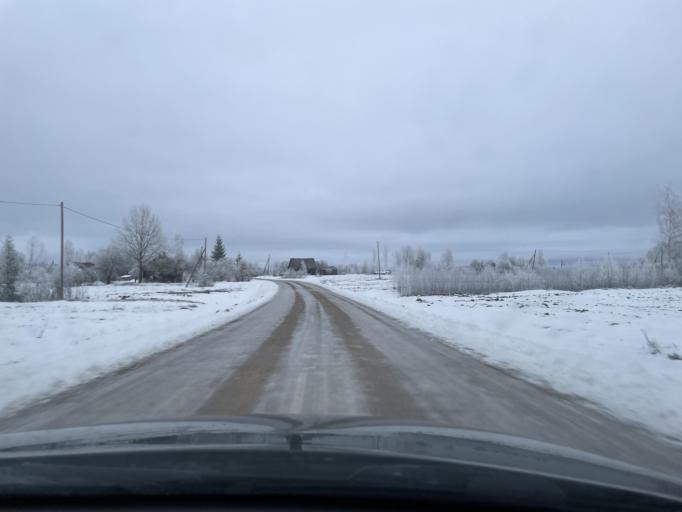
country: LV
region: Ludzas Rajons
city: Ludza
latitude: 56.4655
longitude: 27.5836
